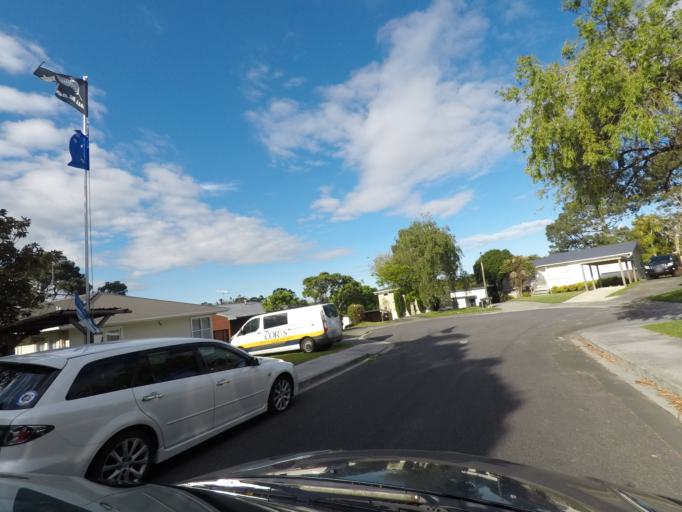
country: NZ
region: Auckland
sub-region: Auckland
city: Rosebank
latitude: -36.8826
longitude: 174.6535
